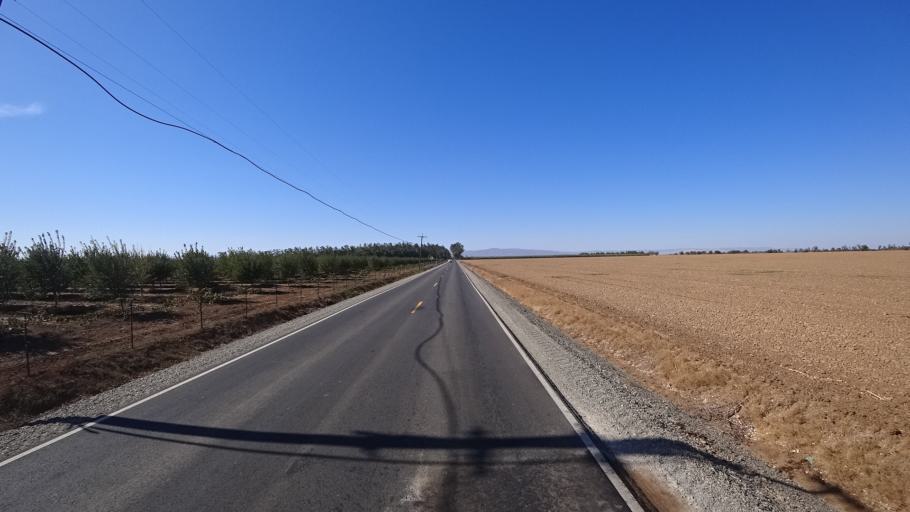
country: US
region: California
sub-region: Yolo County
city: Woodland
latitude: 38.6197
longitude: -121.8594
